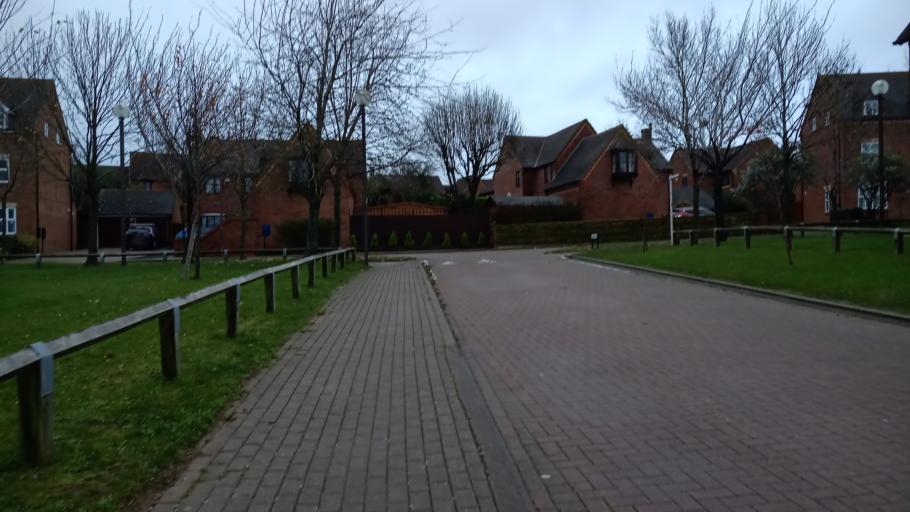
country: GB
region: England
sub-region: Milton Keynes
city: Shenley Church End
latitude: 52.0118
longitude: -0.7897
